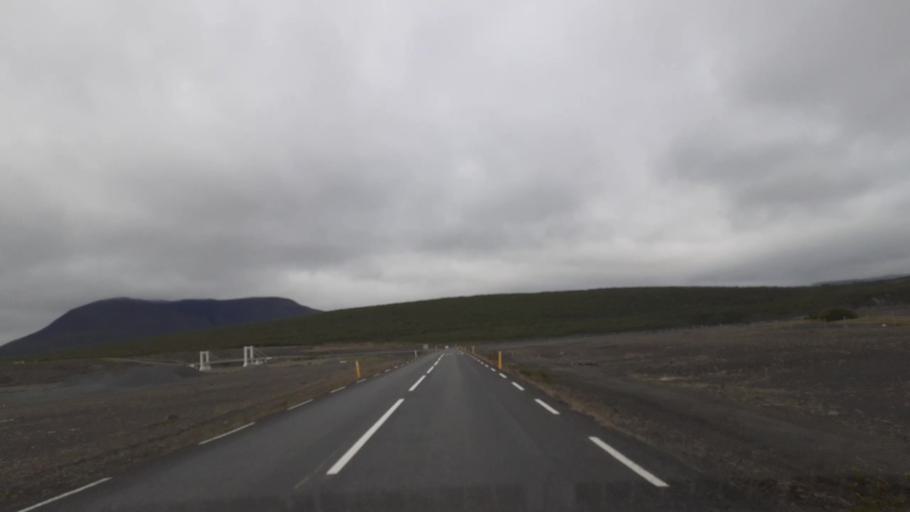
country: IS
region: Northeast
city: Husavik
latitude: 66.0308
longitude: -16.4576
